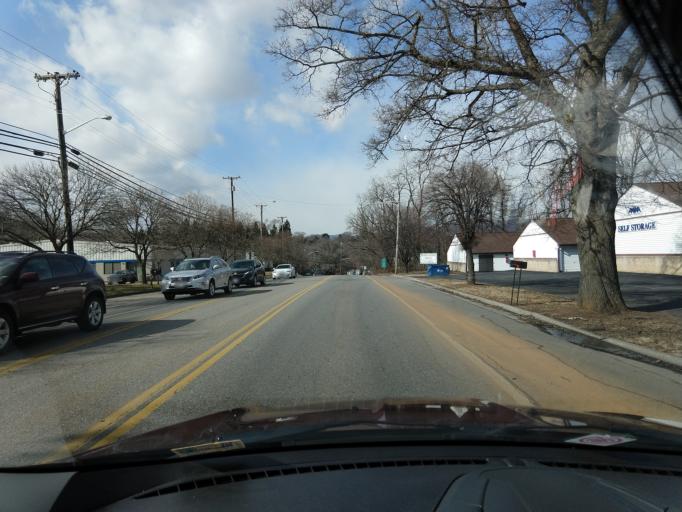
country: US
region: Virginia
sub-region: City of Salem
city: Salem
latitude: 37.2735
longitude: -80.0504
